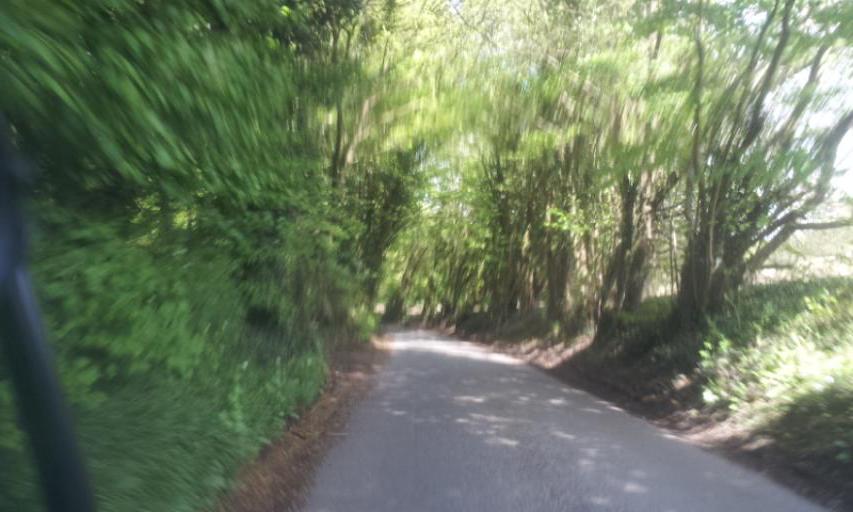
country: GB
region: England
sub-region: Medway
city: Halling
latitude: 51.3783
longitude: 0.4126
